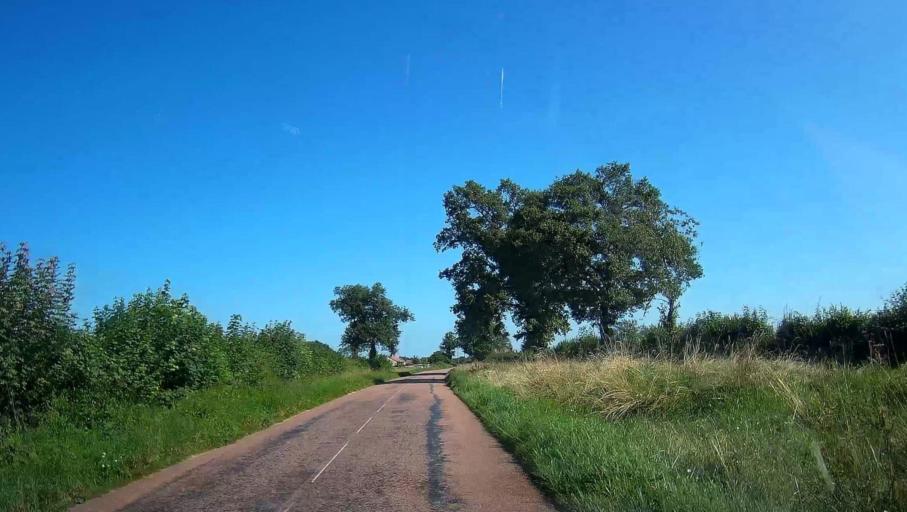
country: FR
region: Bourgogne
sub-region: Departement de Saone-et-Loire
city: Couches
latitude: 46.8787
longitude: 4.5334
